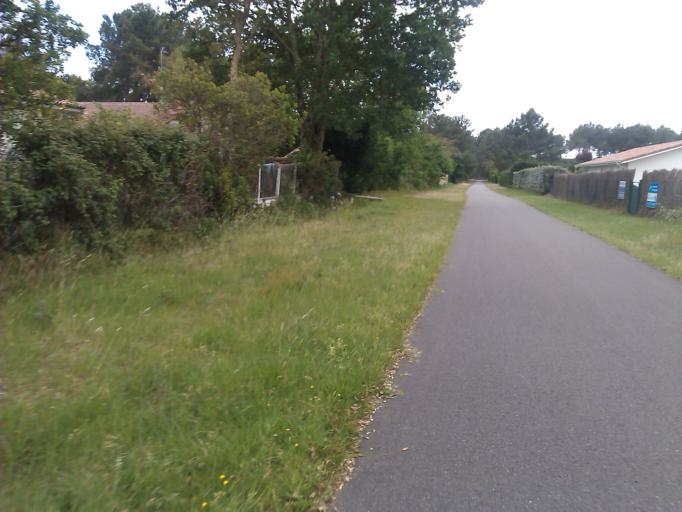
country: FR
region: Aquitaine
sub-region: Departement des Landes
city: Leon
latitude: 43.8464
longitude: -1.3537
